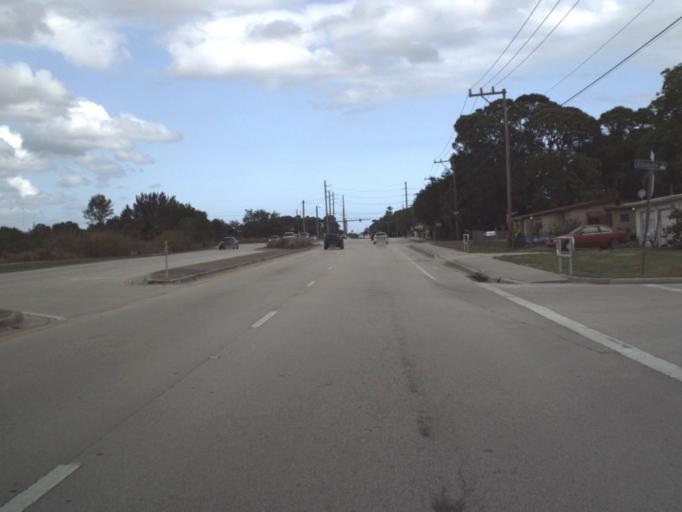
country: US
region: Florida
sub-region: Saint Lucie County
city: Fort Pierce South
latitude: 27.4079
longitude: -80.3498
